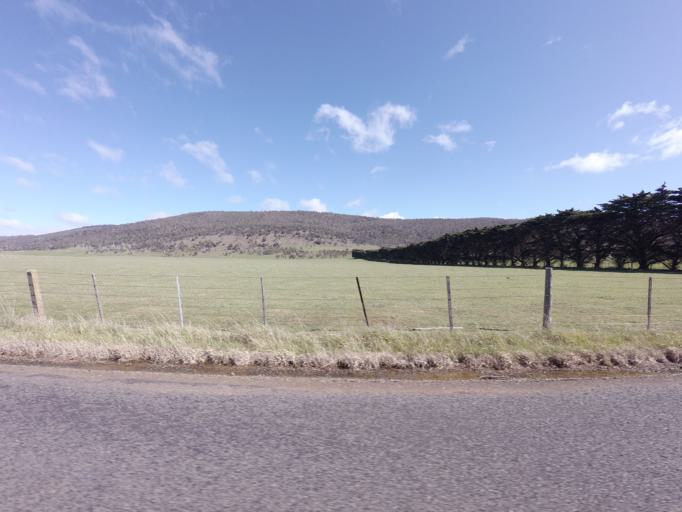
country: AU
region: Tasmania
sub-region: Northern Midlands
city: Evandale
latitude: -41.9665
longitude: 147.4412
